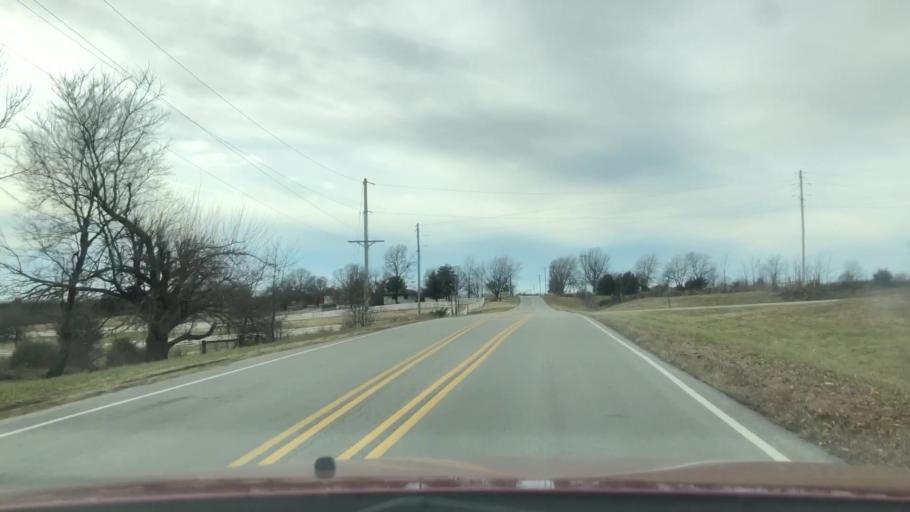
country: US
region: Missouri
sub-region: Greene County
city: Springfield
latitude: 37.2729
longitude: -93.2363
